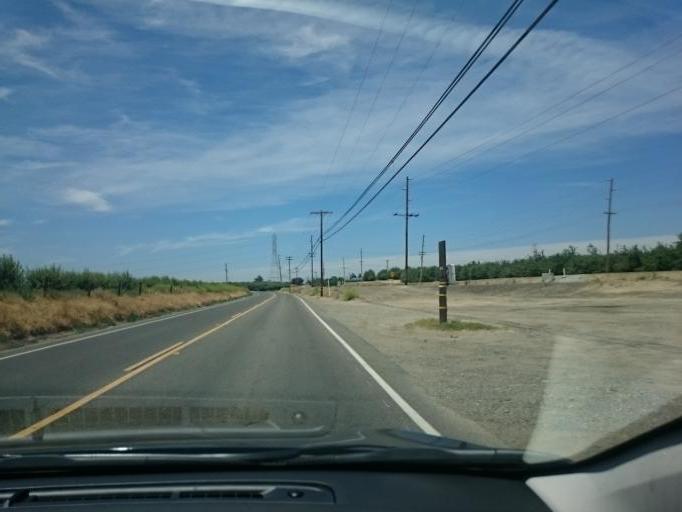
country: US
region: California
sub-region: Stanislaus County
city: Waterford
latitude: 37.6413
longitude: -120.7256
